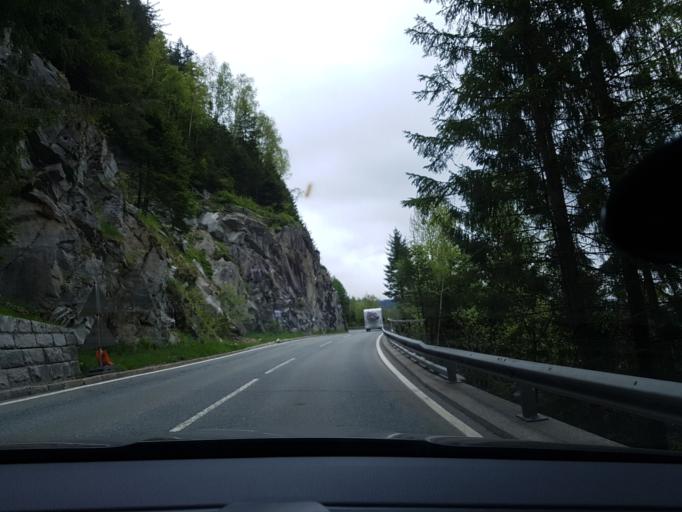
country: AT
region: Salzburg
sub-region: Politischer Bezirk Zell am See
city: Krimml
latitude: 47.2137
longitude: 12.1640
